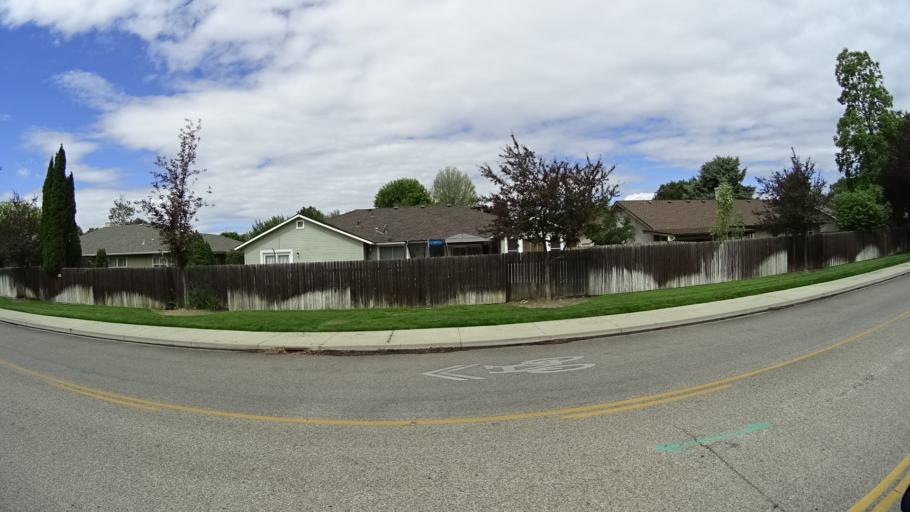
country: US
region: Idaho
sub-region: Ada County
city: Boise
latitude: 43.5688
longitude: -116.1734
